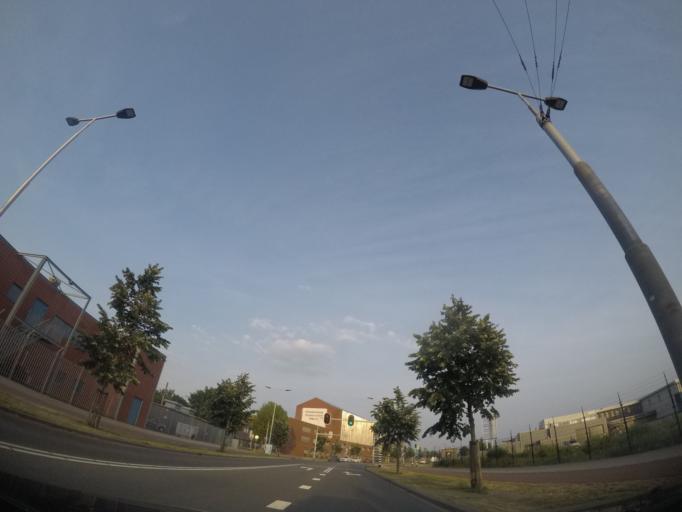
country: NL
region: Gelderland
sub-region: Gemeente Arnhem
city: Arnhem
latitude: 51.9754
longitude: 5.9165
